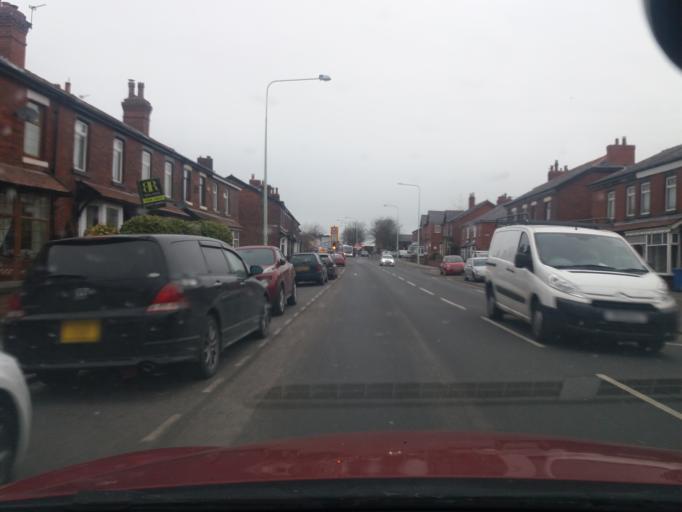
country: GB
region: England
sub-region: Lancashire
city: Chorley
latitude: 53.6599
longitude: -2.6188
